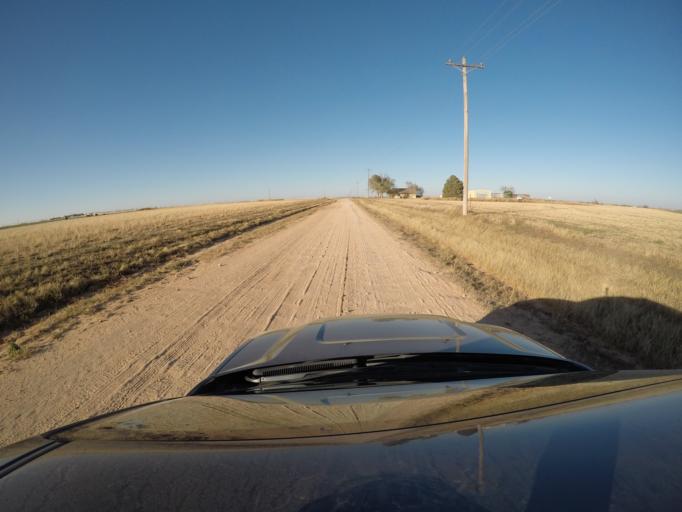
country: US
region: New Mexico
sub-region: Curry County
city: Texico
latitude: 34.3812
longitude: -103.1082
